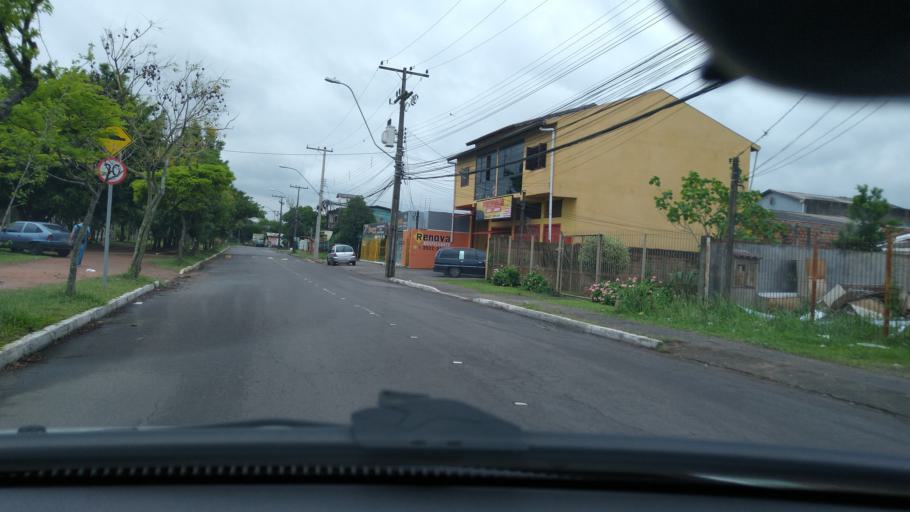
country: BR
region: Rio Grande do Sul
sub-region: Canoas
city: Canoas
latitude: -29.9014
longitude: -51.2036
